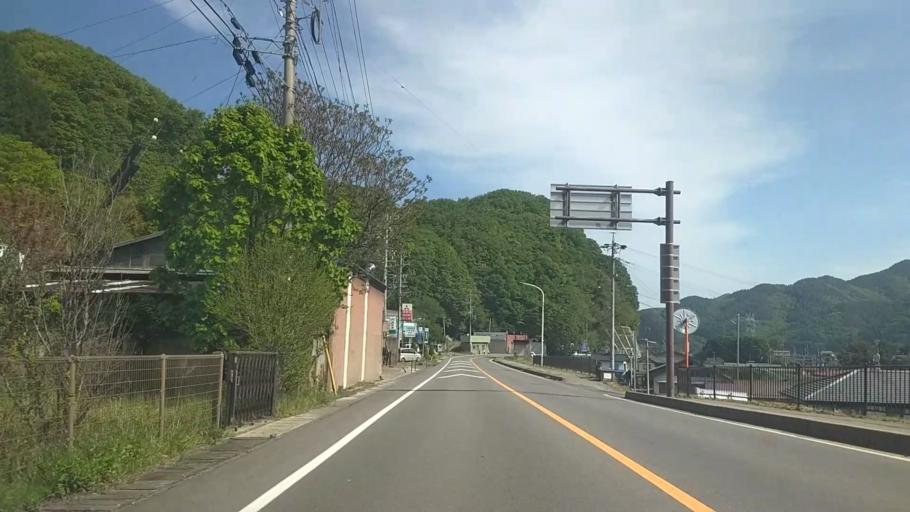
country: JP
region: Nagano
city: Saku
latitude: 36.0961
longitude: 138.4828
